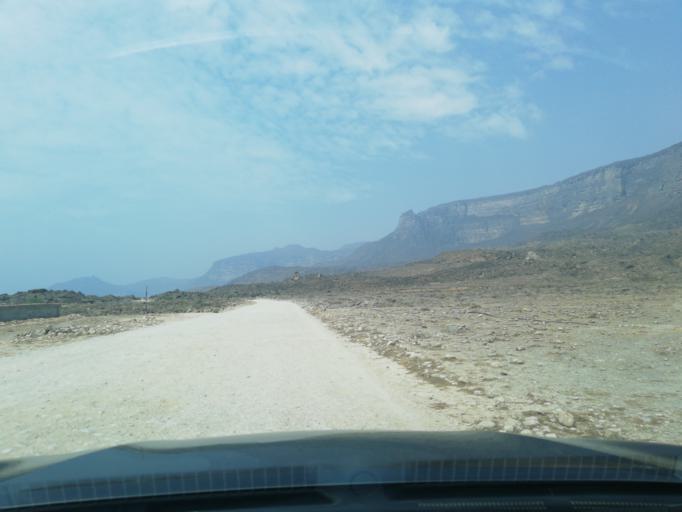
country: OM
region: Zufar
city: Salalah
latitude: 16.8329
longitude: 53.7105
